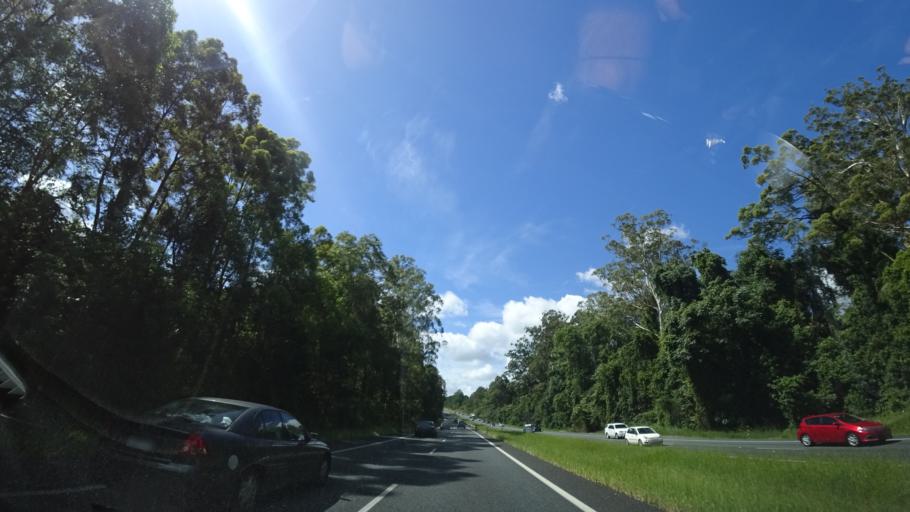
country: AU
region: Queensland
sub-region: Sunshine Coast
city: Woombye
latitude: -26.6663
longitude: 152.9969
